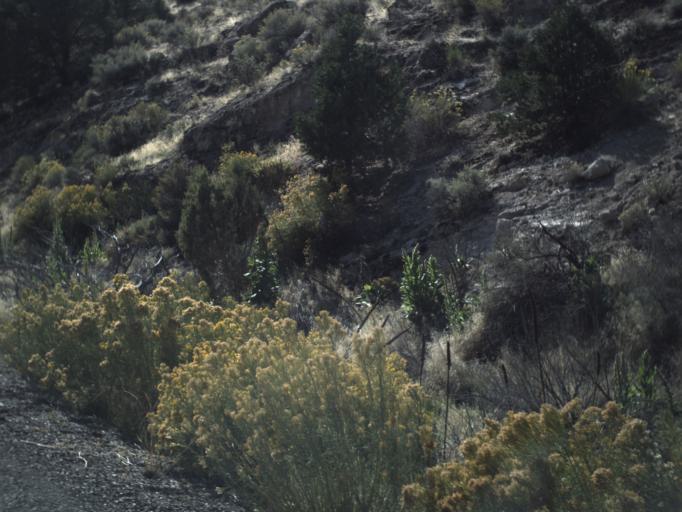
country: US
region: Utah
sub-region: Sevier County
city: Monroe
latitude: 38.5715
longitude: -112.3514
